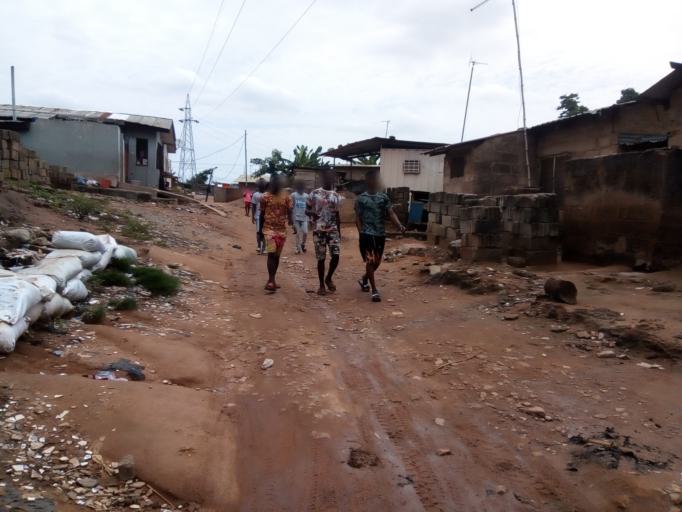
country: GH
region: Eastern
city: Nsawam
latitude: 5.7795
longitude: -0.3360
